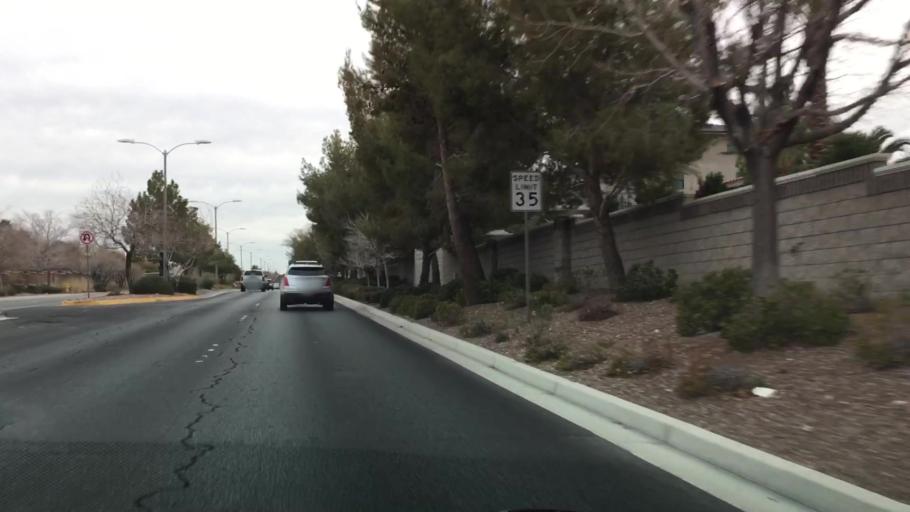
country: US
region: Nevada
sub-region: Clark County
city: Whitney
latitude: 35.9774
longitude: -115.1010
